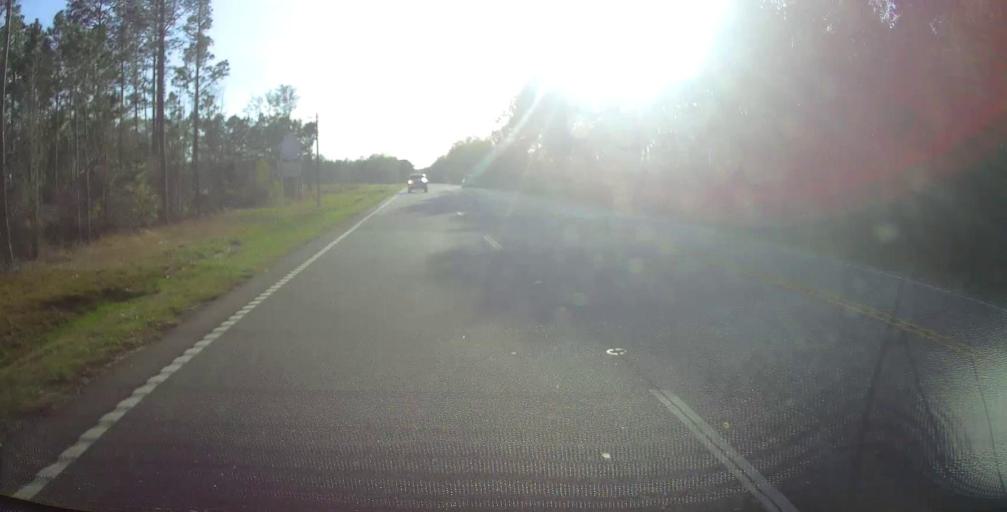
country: US
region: Georgia
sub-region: Tattnall County
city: Reidsville
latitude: 32.1039
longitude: -82.0959
